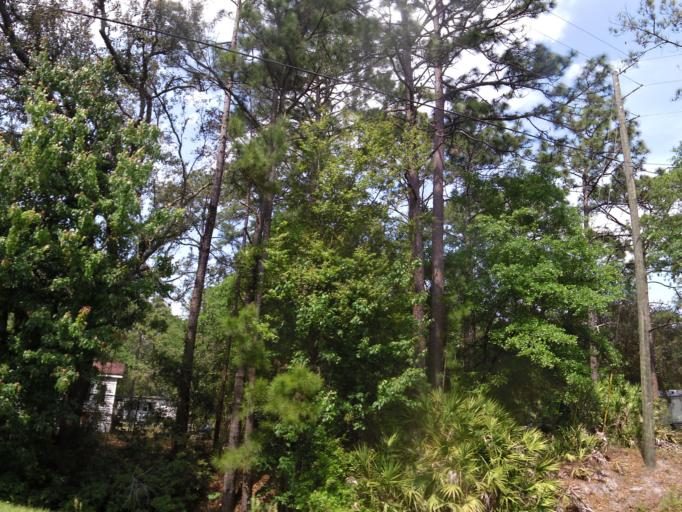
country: US
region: Georgia
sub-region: Camden County
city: Kingsland
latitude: 30.7803
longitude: -81.6827
